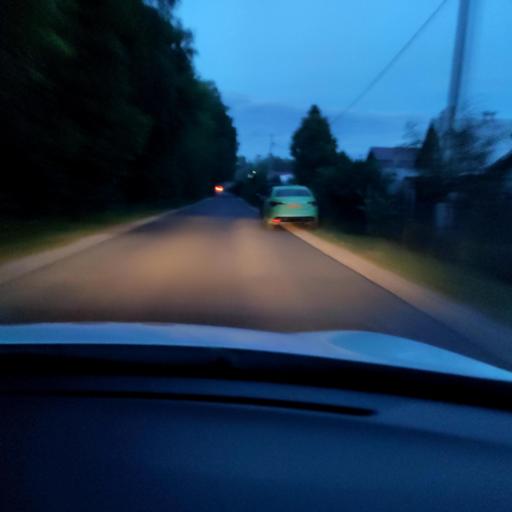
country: RU
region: Tatarstan
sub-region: Gorod Kazan'
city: Kazan
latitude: 55.9470
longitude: 49.0660
